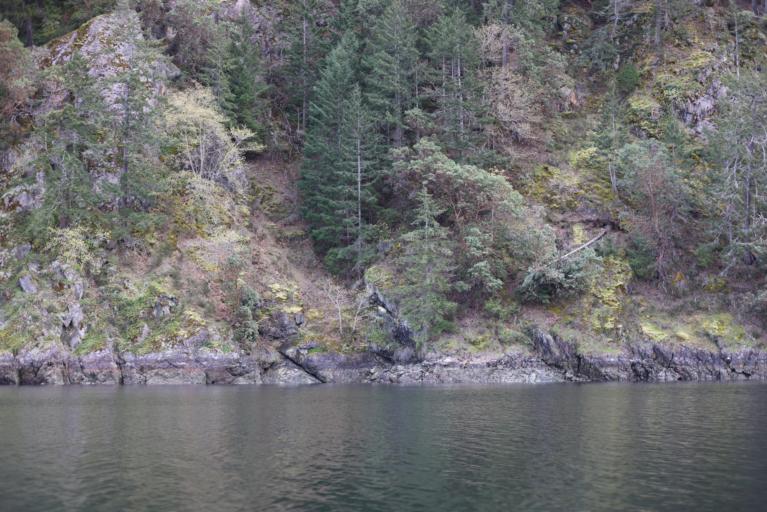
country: CA
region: British Columbia
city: Langford
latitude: 48.5153
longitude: -123.5368
